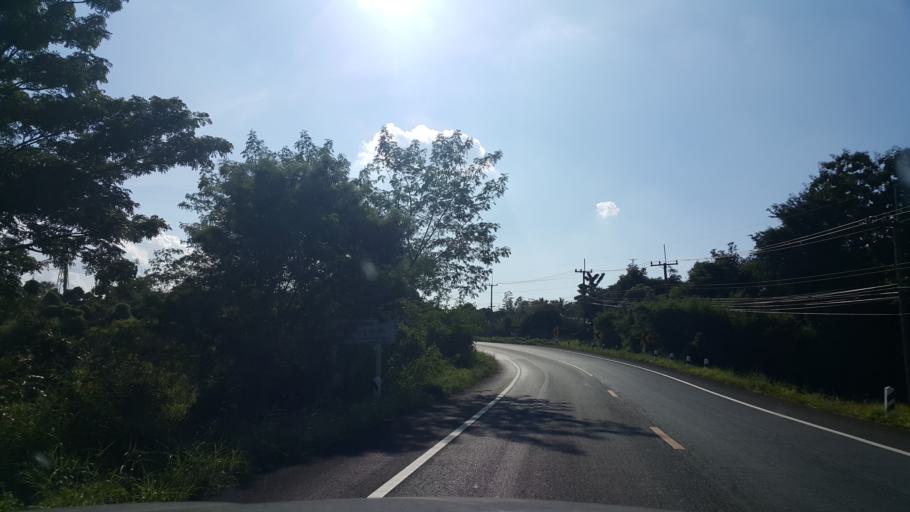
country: TH
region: Lamphun
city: Mae Tha
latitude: 18.4762
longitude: 99.1695
